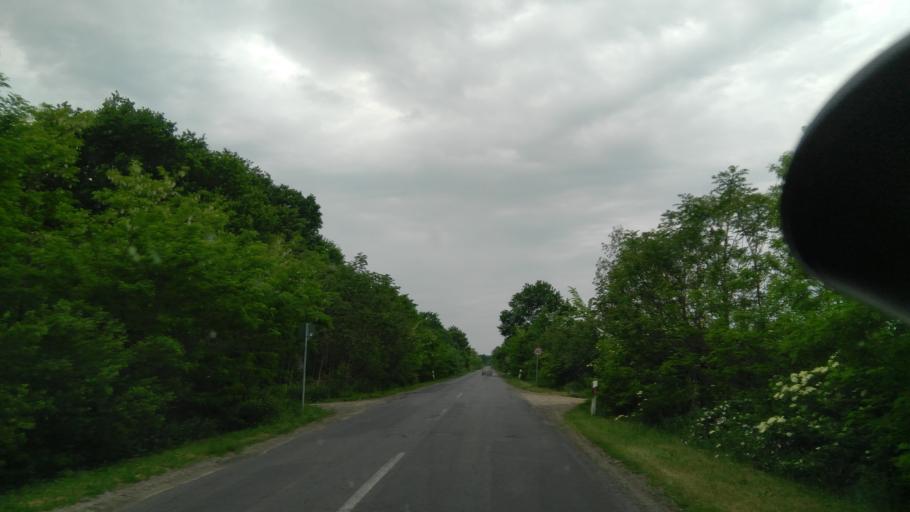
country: HU
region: Bekes
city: Doboz
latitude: 46.7209
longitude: 21.3140
